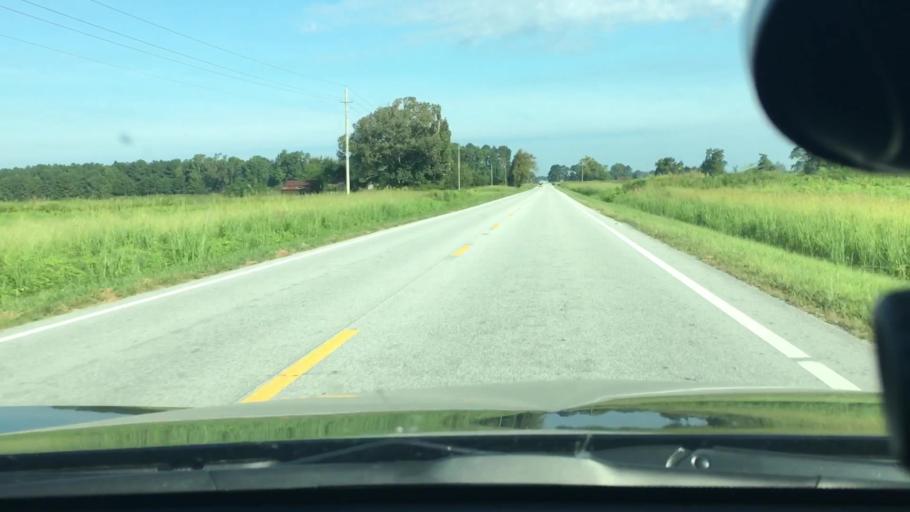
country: US
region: North Carolina
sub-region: Pitt County
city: Summerfield
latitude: 35.6589
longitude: -77.4713
